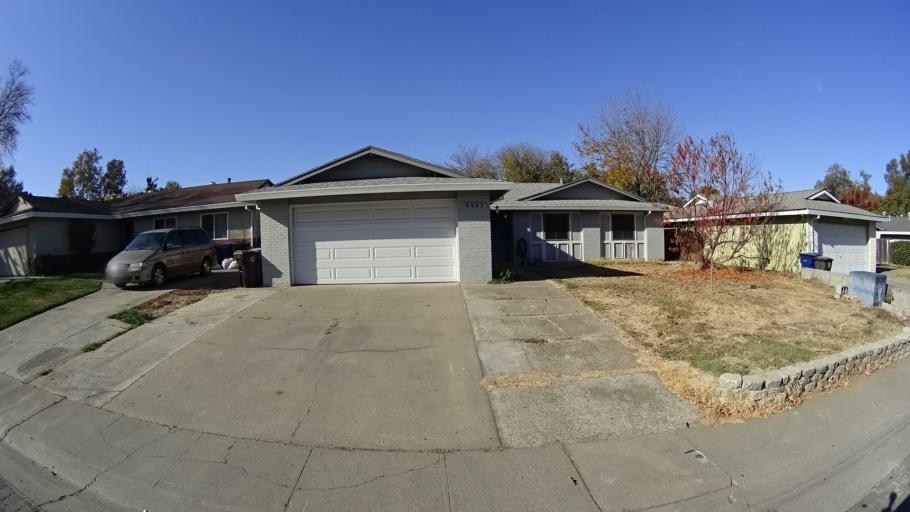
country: US
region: California
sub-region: Sacramento County
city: Citrus Heights
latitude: 38.6743
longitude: -121.3033
